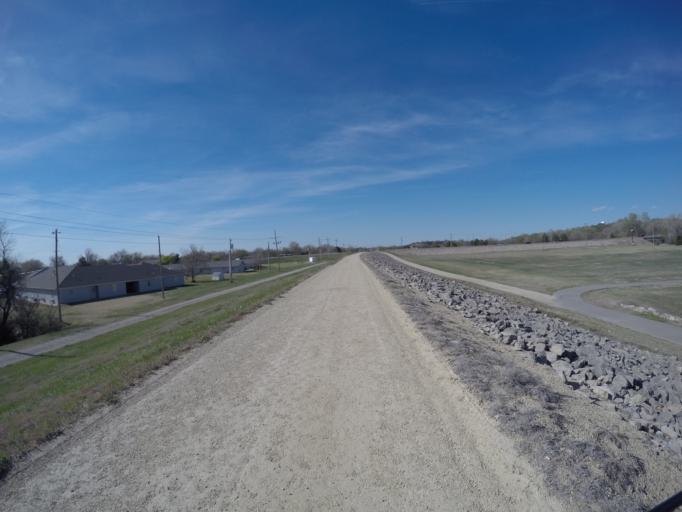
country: US
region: Kansas
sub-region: Saline County
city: Salina
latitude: 38.8253
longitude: -97.5881
